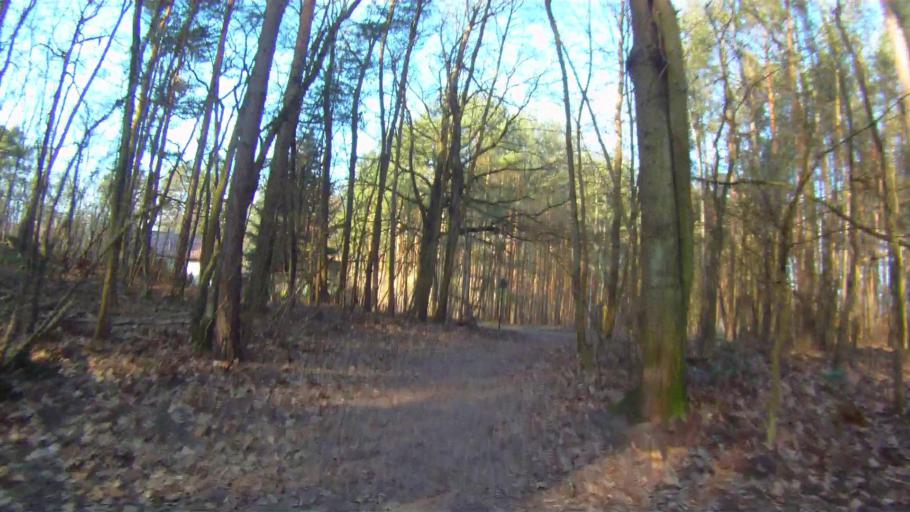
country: DE
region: Brandenburg
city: Woltersdorf
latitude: 52.4641
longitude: 13.7316
